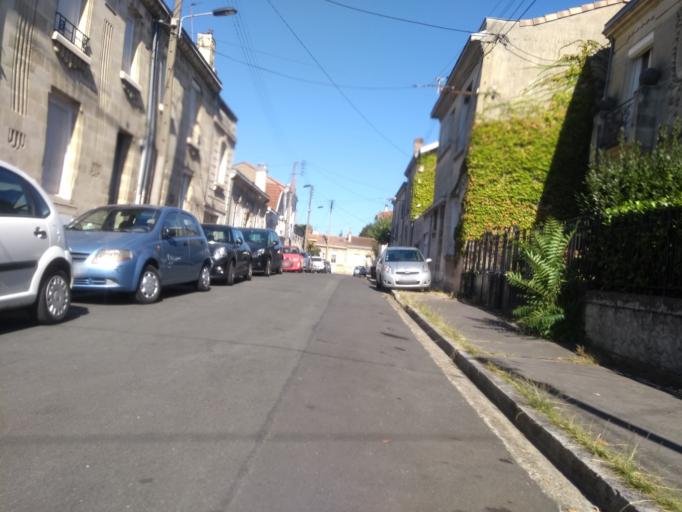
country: FR
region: Aquitaine
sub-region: Departement de la Gironde
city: Merignac
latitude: 44.8387
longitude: -0.6093
